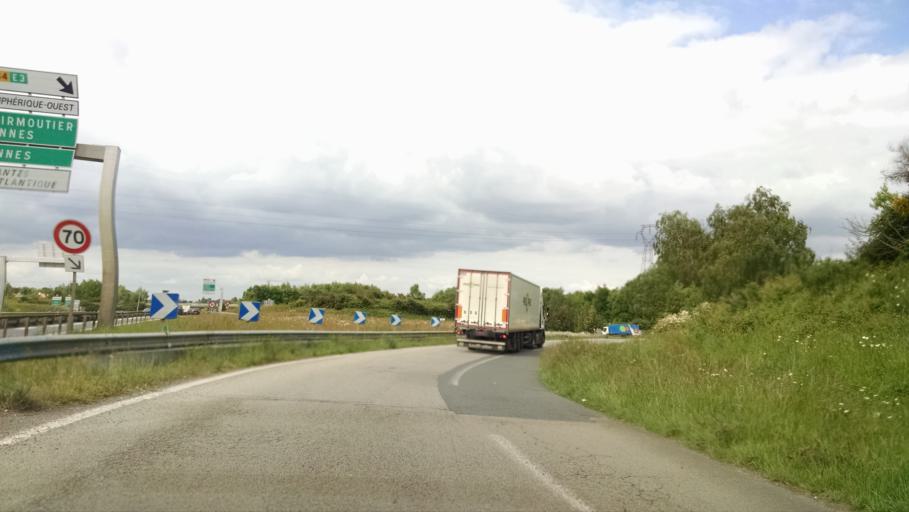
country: FR
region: Pays de la Loire
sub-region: Departement de la Loire-Atlantique
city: Les Sorinieres
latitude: 47.1716
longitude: -1.5140
